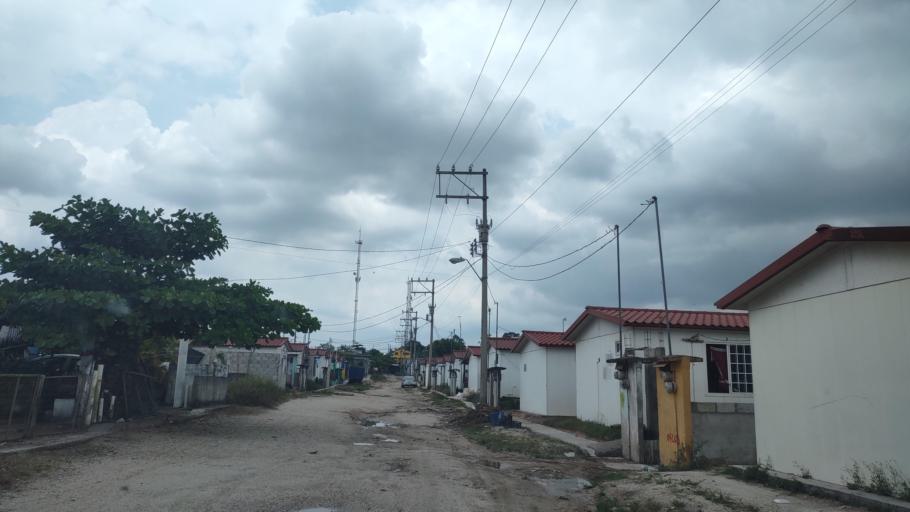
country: MX
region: Veracruz
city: Las Choapas
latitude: 17.9080
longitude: -94.1114
